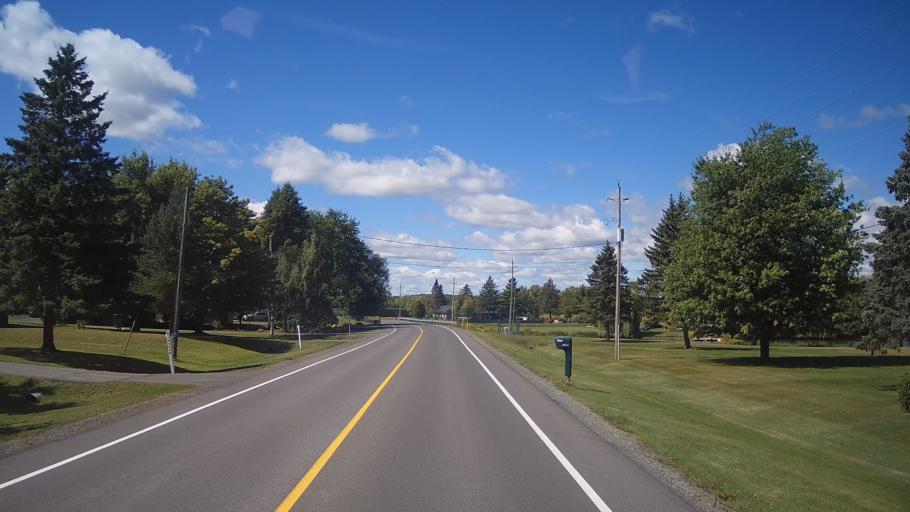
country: US
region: New York
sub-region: St. Lawrence County
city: Norfolk
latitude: 44.8741
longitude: -75.2373
